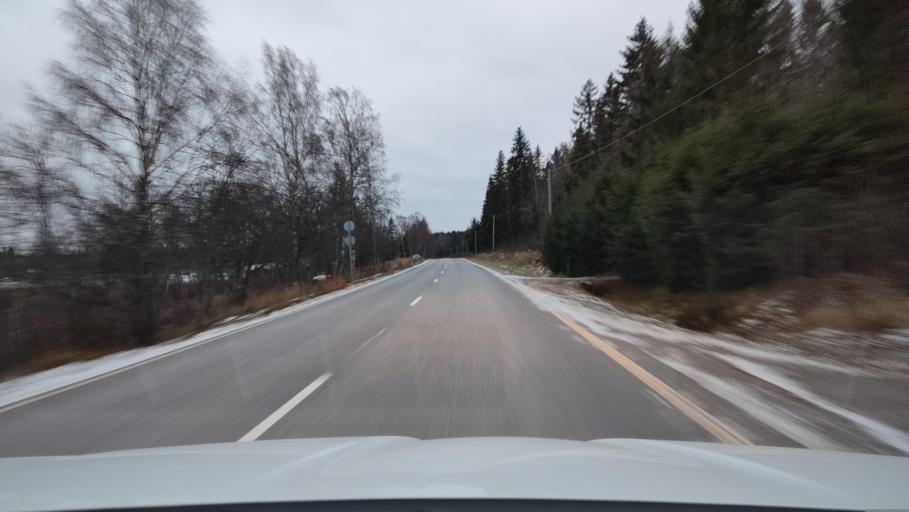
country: FI
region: Ostrobothnia
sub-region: Vaasa
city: Replot
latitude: 63.2707
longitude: 21.3452
